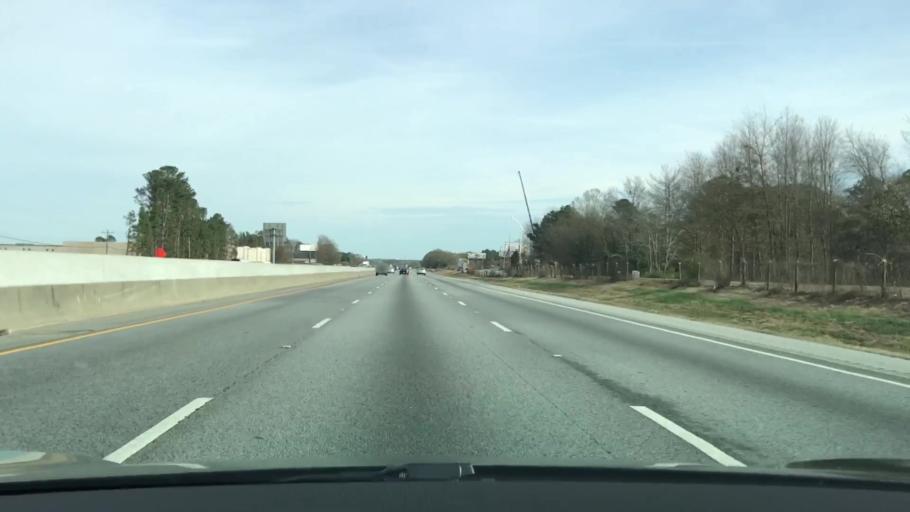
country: US
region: Georgia
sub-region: Rockdale County
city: Conyers
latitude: 33.6317
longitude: -83.9693
